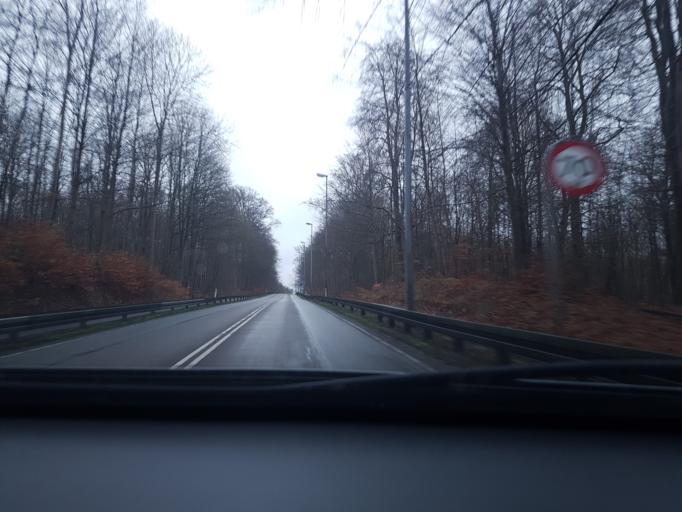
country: DK
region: Capital Region
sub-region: Fureso Kommune
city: Vaerlose
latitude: 55.7586
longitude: 12.3703
